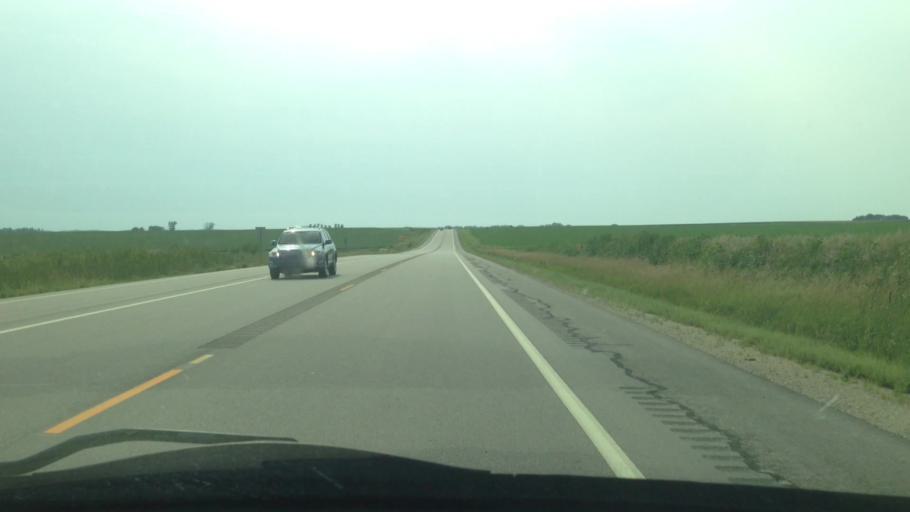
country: US
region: Minnesota
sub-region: Olmsted County
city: Eyota
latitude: 43.9991
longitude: -92.2594
